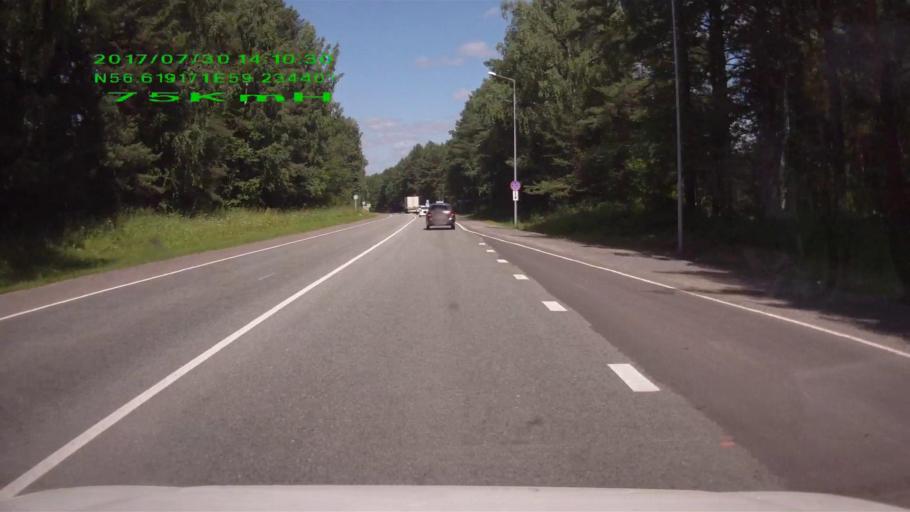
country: RU
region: Sverdlovsk
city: Nizhniye Sergi
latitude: 56.6194
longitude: 59.2347
